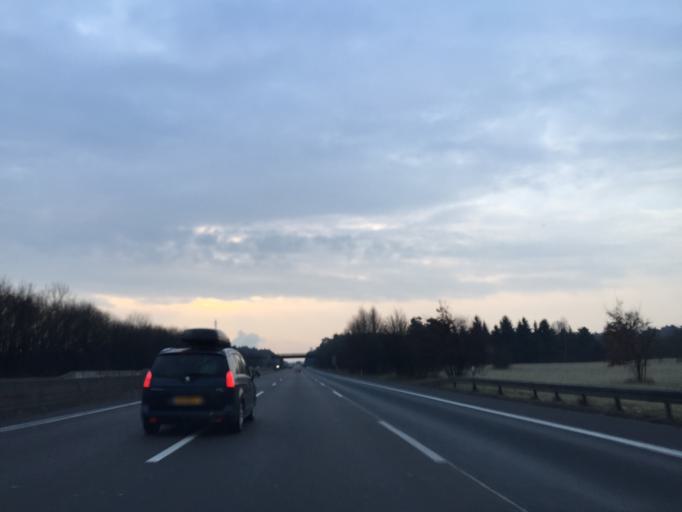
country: DE
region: Hesse
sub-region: Regierungsbezirk Darmstadt
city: Seligenstadt
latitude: 50.0066
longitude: 8.9834
